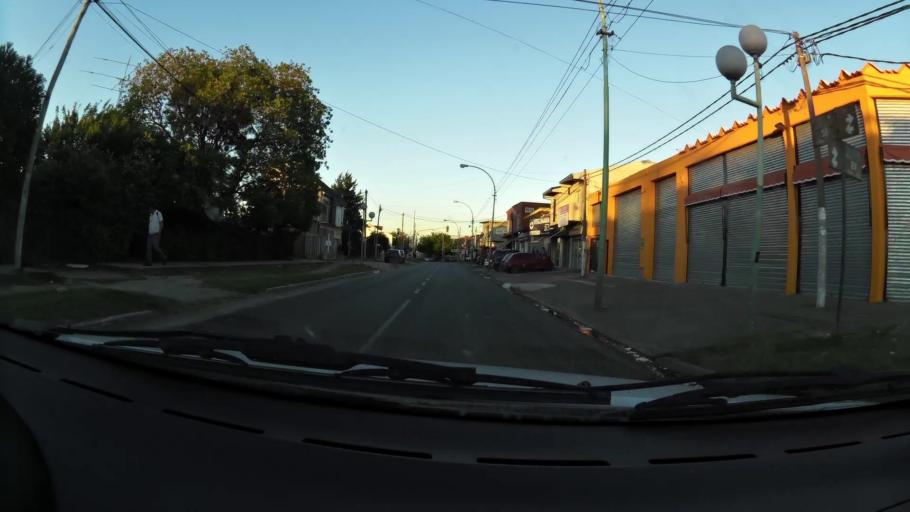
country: AR
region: Buenos Aires
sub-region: Partido de Quilmes
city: Quilmes
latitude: -34.8126
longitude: -58.1895
